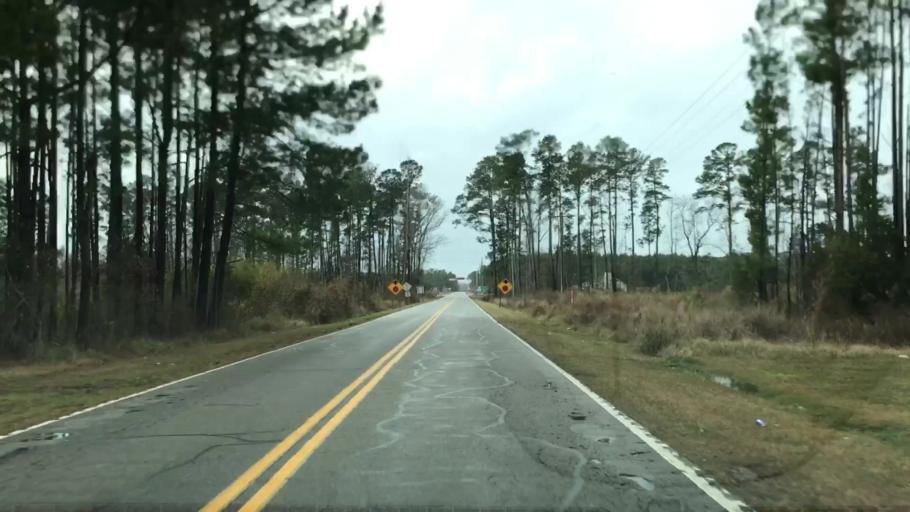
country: US
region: South Carolina
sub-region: Florence County
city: Johnsonville
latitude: 33.6695
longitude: -79.3146
